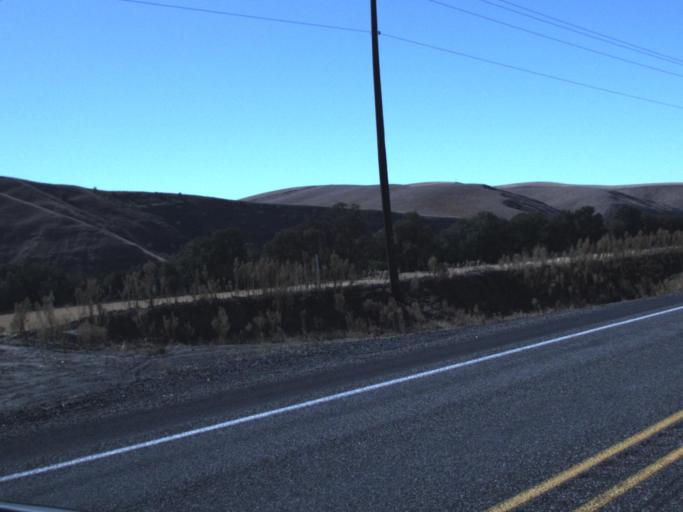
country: US
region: Washington
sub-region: Walla Walla County
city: Waitsburg
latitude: 46.2789
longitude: -118.2283
